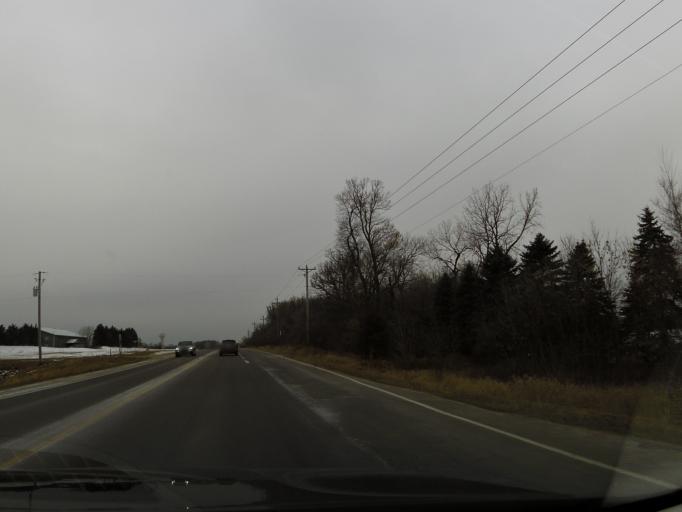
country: US
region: Minnesota
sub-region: Carver County
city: Young America (historical)
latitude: 44.7681
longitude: -93.8978
